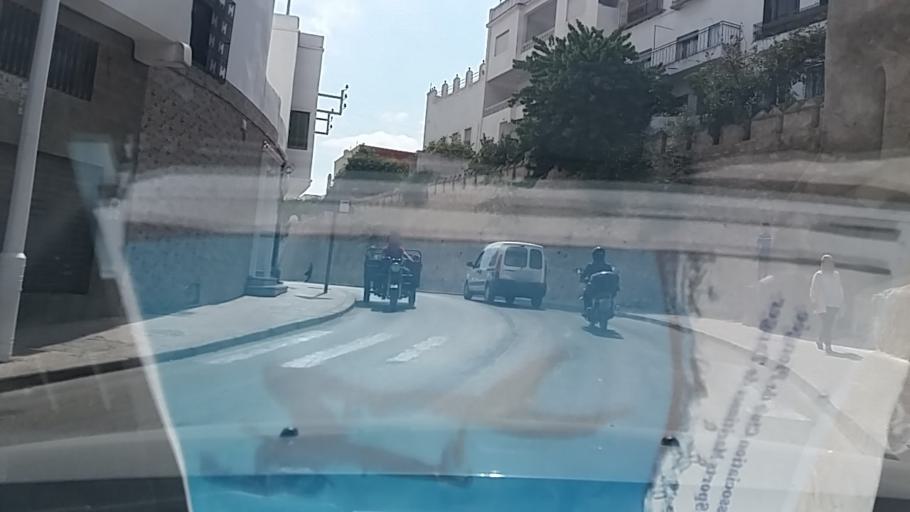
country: MA
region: Tanger-Tetouan
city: Tetouan
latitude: 35.5742
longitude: -5.3638
